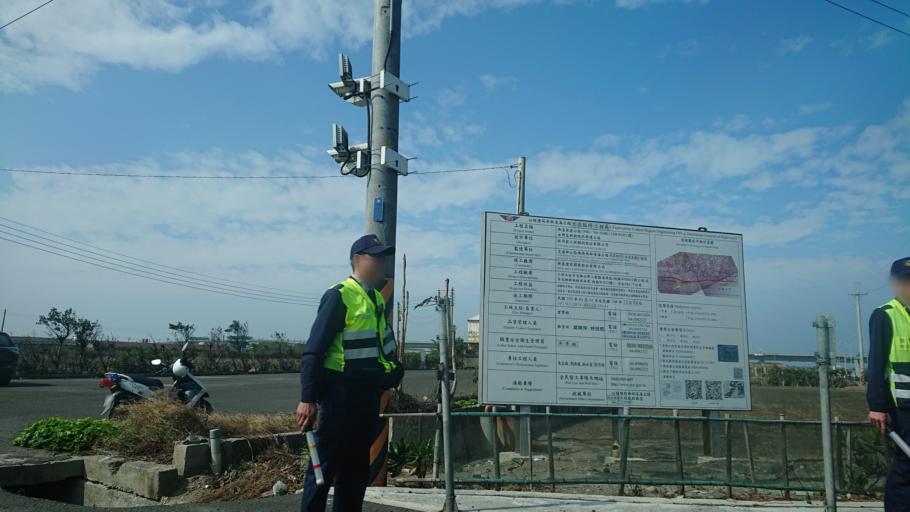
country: TW
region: Taiwan
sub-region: Changhua
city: Chang-hua
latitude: 23.9377
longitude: 120.3251
